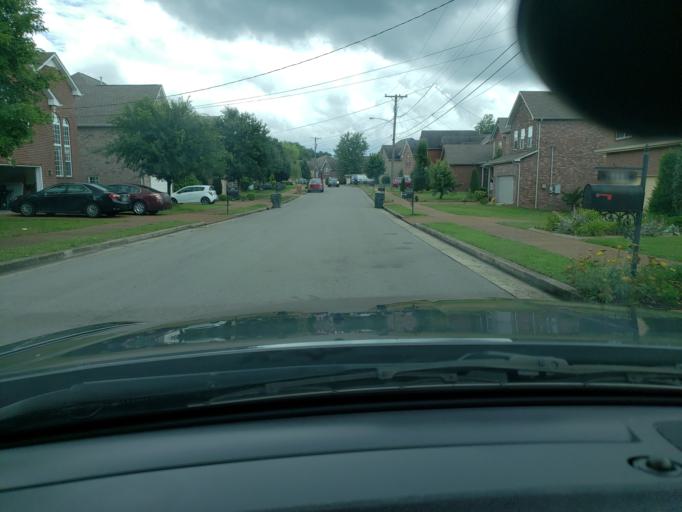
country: US
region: Tennessee
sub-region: Williamson County
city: Nolensville
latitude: 36.0199
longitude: -86.6991
